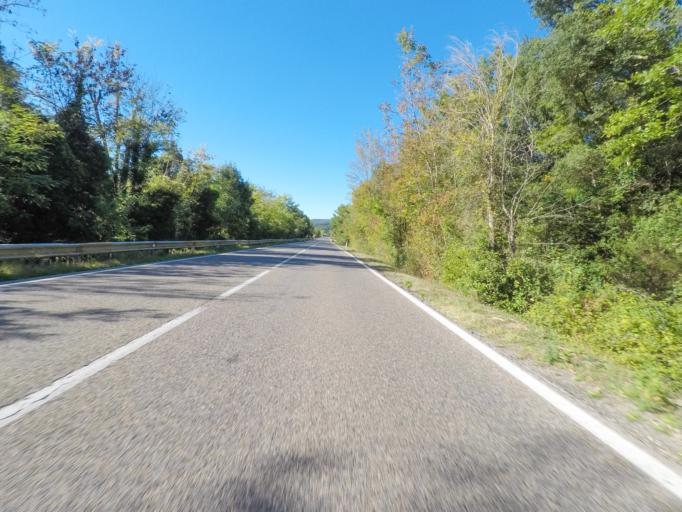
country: IT
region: Tuscany
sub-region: Provincia di Grosseto
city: Civitella Marittima
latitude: 43.0185
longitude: 11.2846
